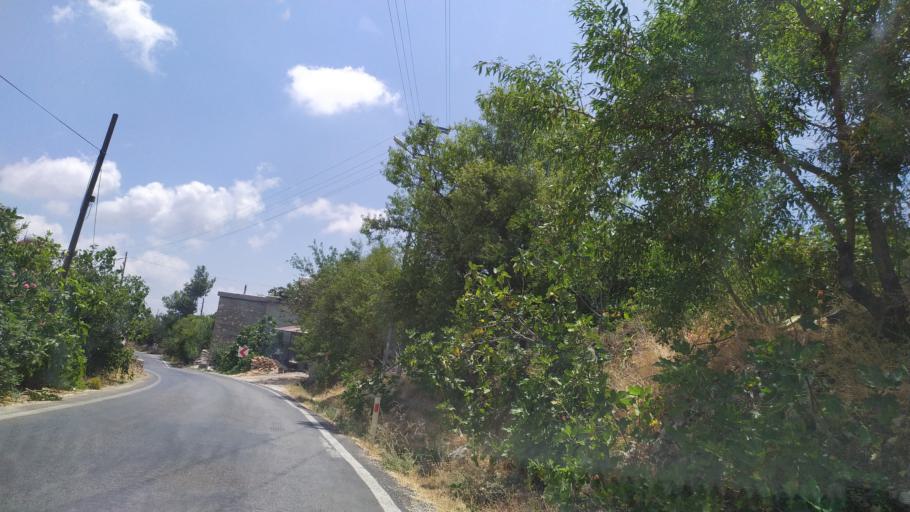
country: TR
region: Mersin
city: Gulnar
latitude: 36.2857
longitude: 33.3836
